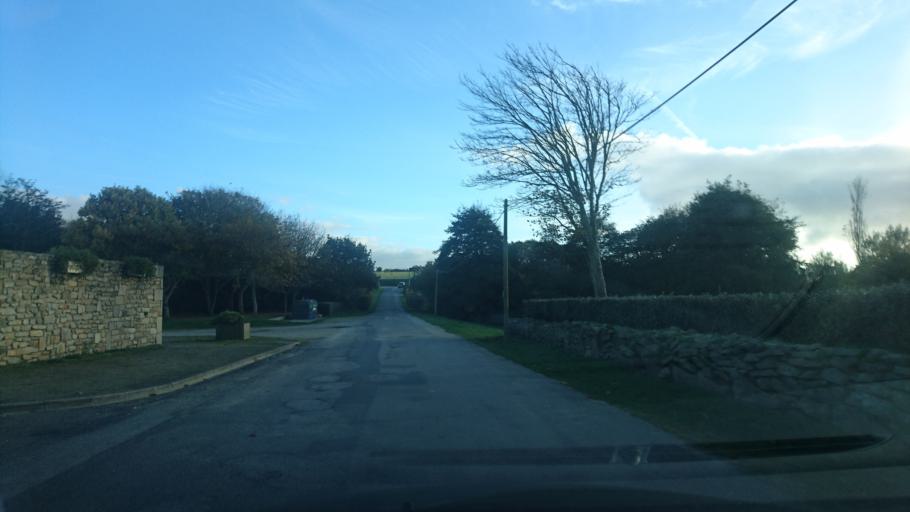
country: FR
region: Brittany
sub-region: Departement du Finistere
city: Lampaul-Plouarzel
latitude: 48.4237
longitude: -4.7678
